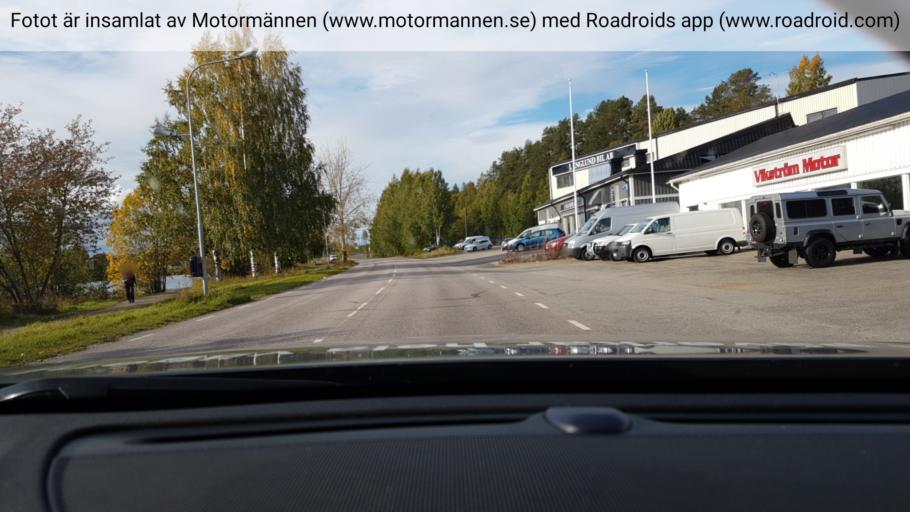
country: SE
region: Norrbotten
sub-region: Lulea Kommun
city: Lulea
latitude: 65.6056
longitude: 22.1318
